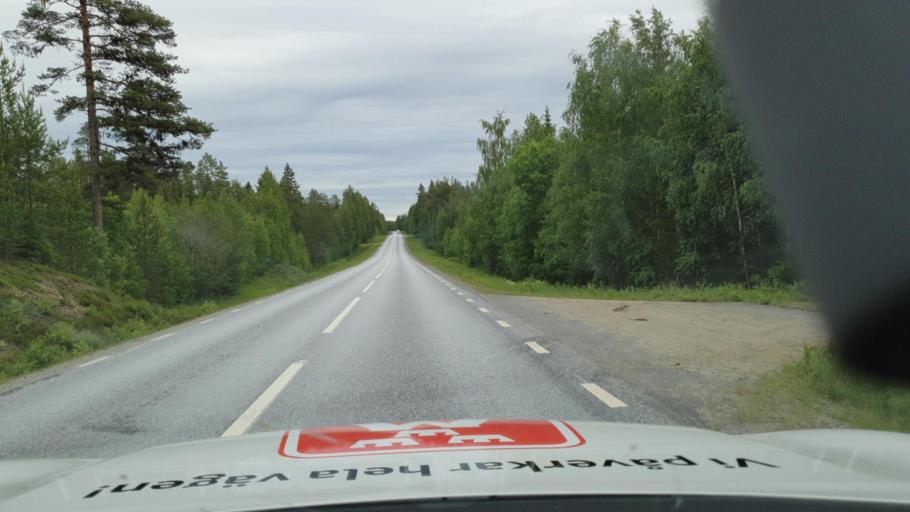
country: SE
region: Vaesterbotten
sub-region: Bjurholms Kommun
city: Bjurholm
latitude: 64.0062
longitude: 18.7241
